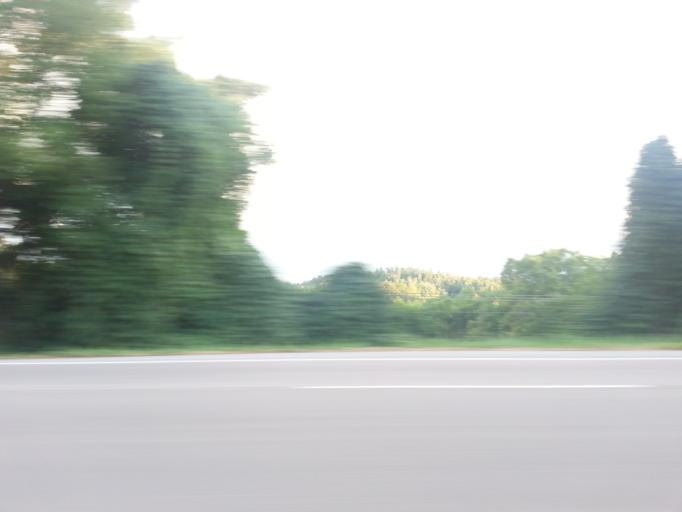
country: US
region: Tennessee
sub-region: Knox County
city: Mascot
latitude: 36.0556
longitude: -83.6986
